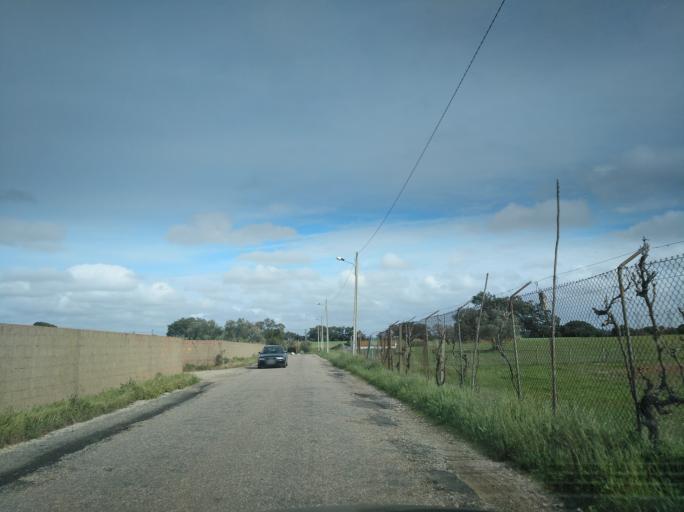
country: PT
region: Setubal
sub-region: Grandola
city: Grandola
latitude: 38.1877
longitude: -8.5584
